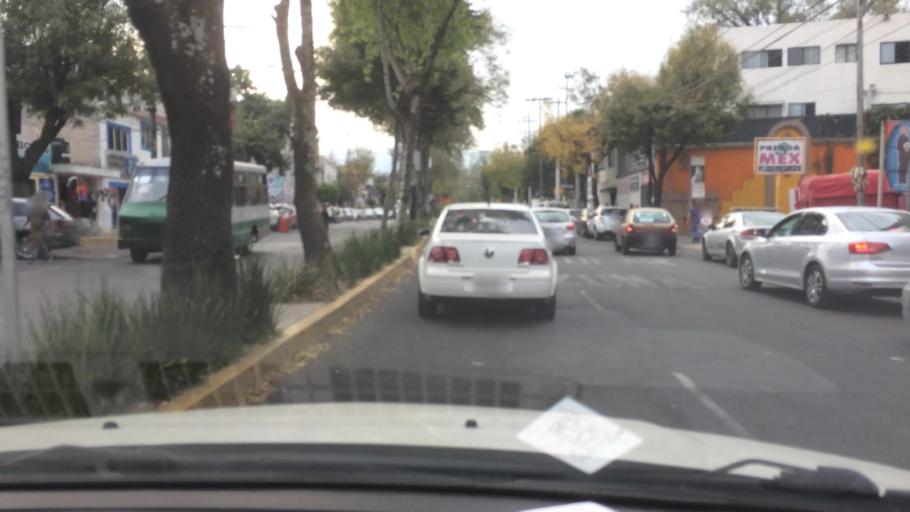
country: MX
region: Mexico City
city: Tlalpan
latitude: 19.2953
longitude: -99.1798
